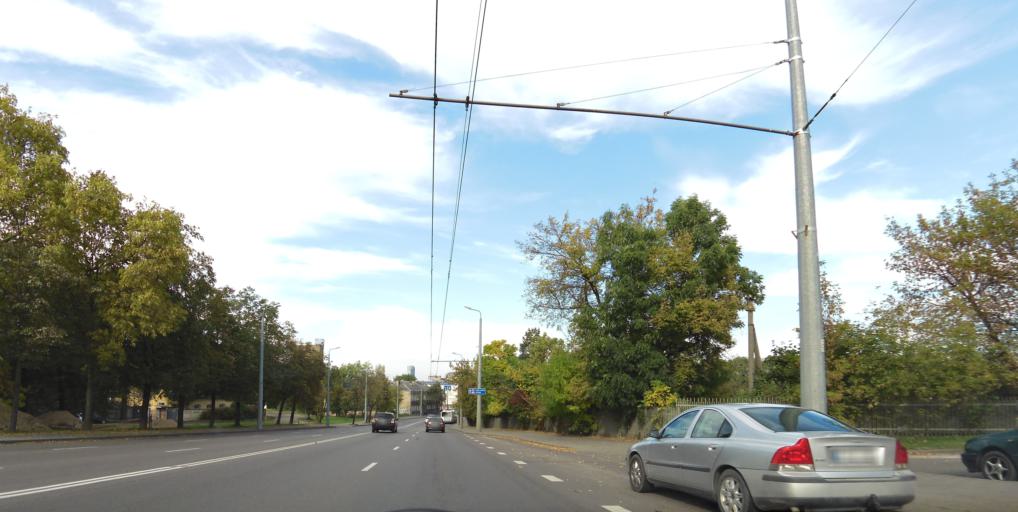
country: LT
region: Vilnius County
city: Naujamiestis
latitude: 54.6675
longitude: 25.2721
